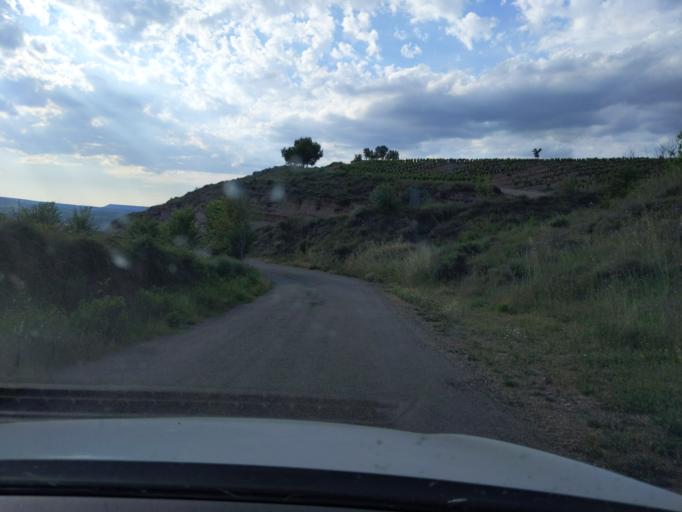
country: ES
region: La Rioja
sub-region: Provincia de La Rioja
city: Albelda de Iregua
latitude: 42.3546
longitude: -2.4645
